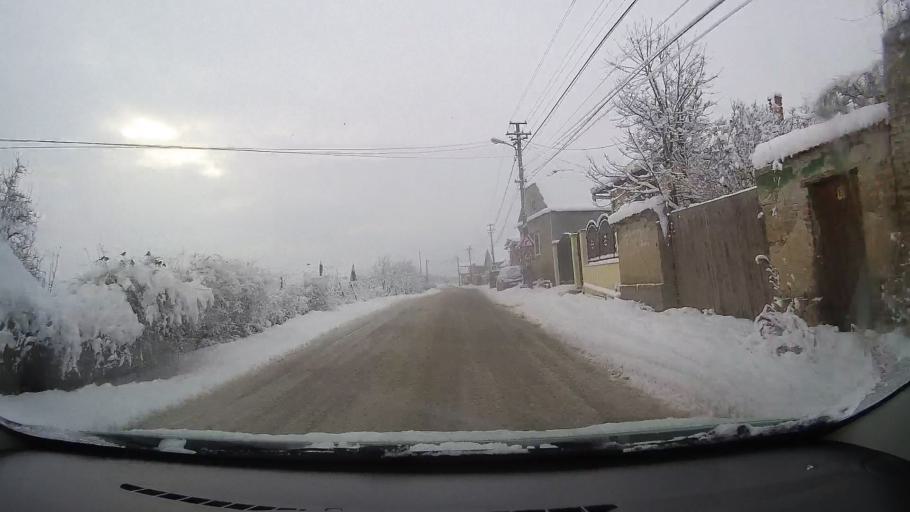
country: RO
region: Alba
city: Vurpar
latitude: 45.9747
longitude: 23.4807
